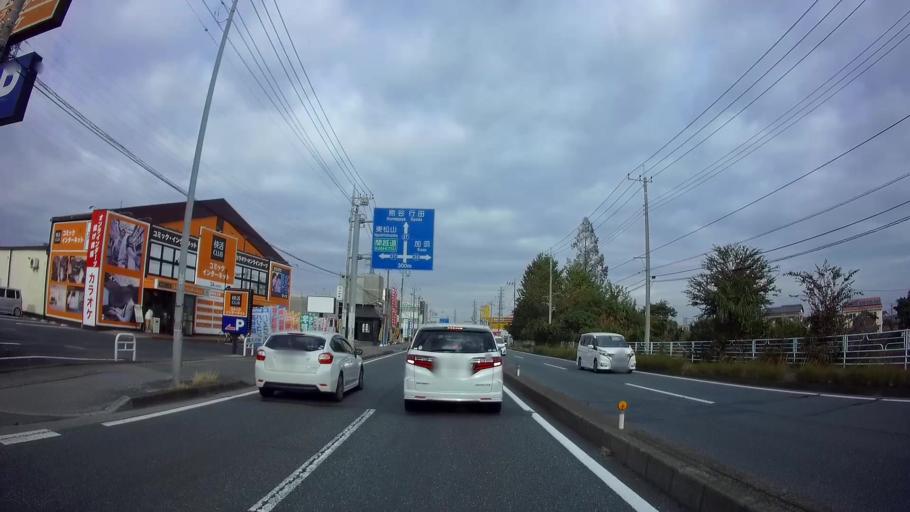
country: JP
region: Saitama
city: Konosu
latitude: 36.0567
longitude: 139.5241
